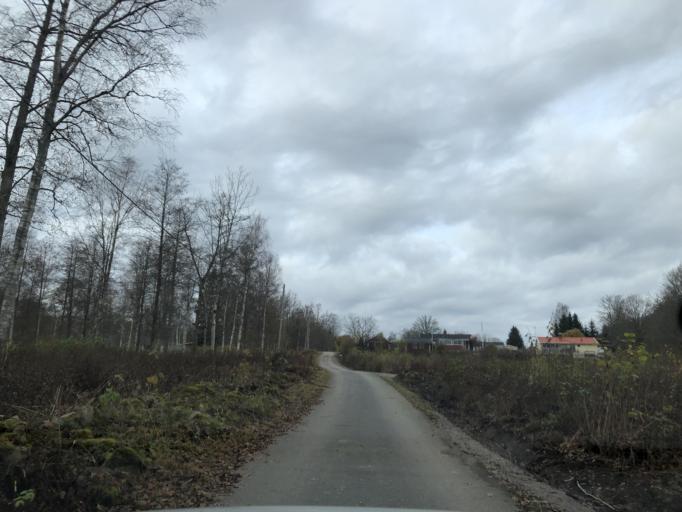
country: SE
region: Vaestra Goetaland
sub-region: Ulricehamns Kommun
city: Ulricehamn
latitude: 57.7150
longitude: 13.3672
